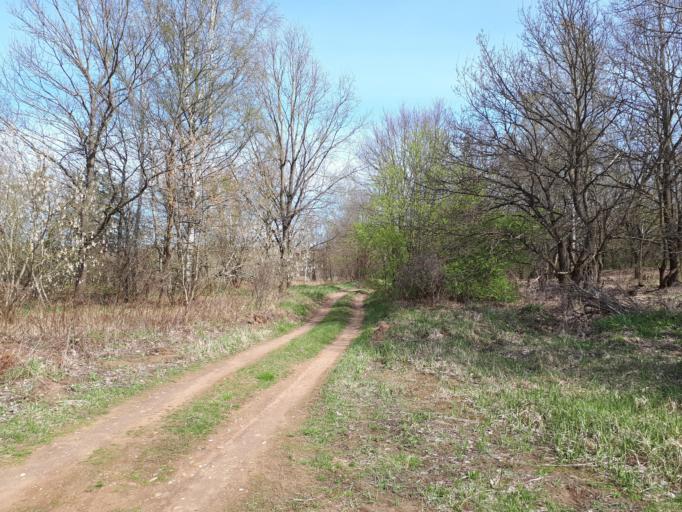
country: LT
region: Kauno apskritis
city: Jonava
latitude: 55.0767
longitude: 24.3344
